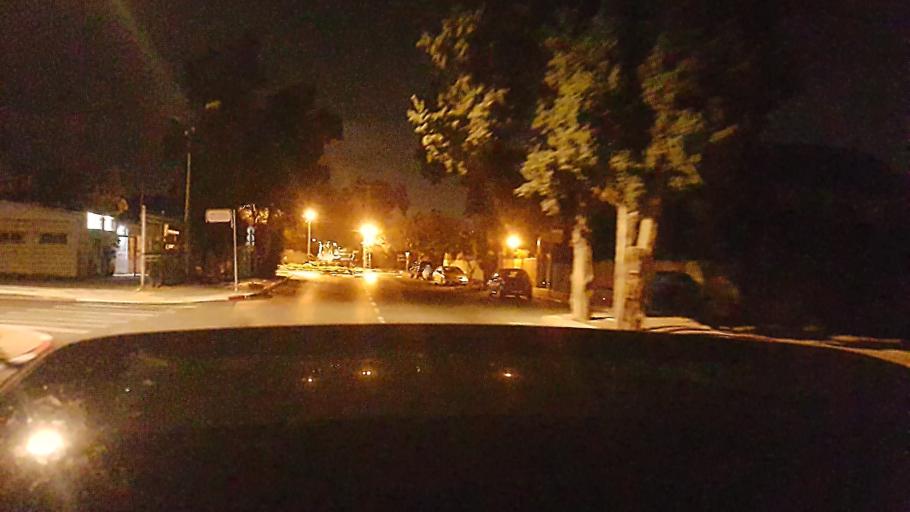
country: IL
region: Central District
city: Hod HaSharon
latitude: 32.1618
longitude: 34.8868
